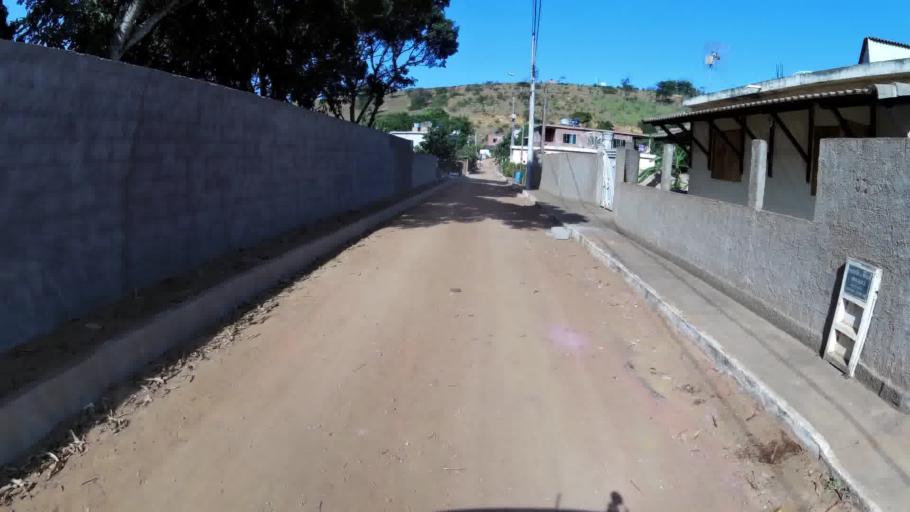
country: BR
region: Espirito Santo
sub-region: Piuma
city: Piuma
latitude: -20.8851
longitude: -40.7763
